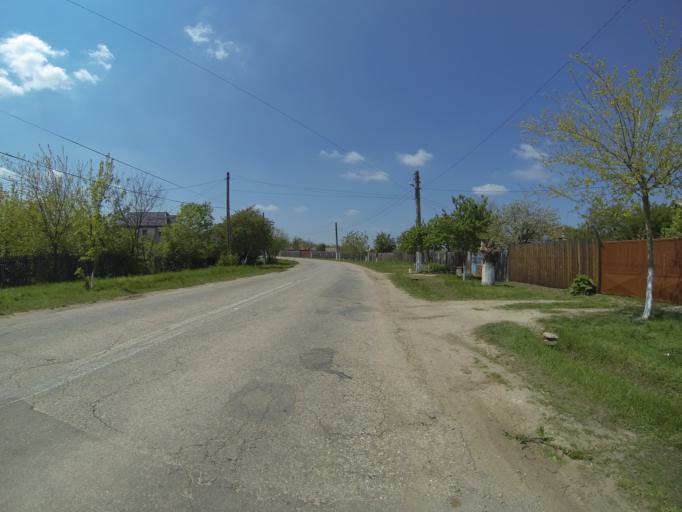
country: RO
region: Dolj
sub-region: Comuna Salcuta
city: Salcuta
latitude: 44.2535
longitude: 23.4228
